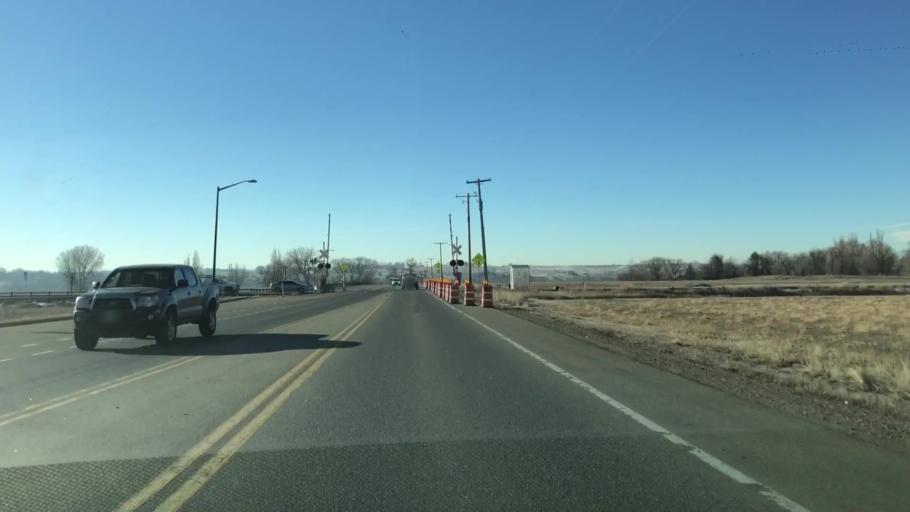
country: US
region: Colorado
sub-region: Larimer County
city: Loveland
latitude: 40.4007
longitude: -105.0212
